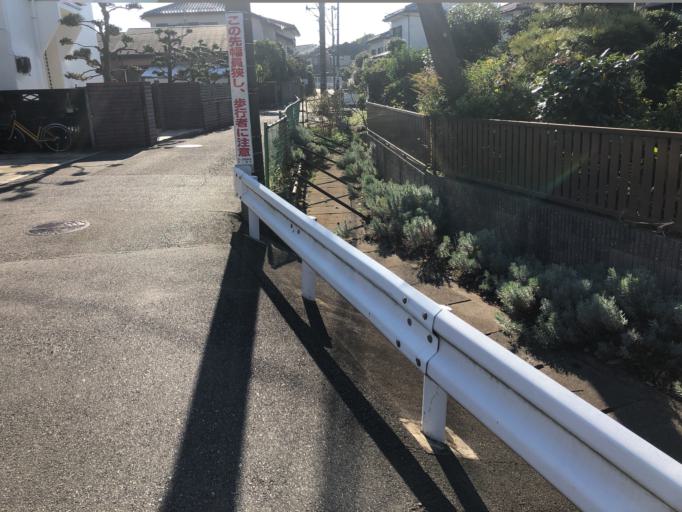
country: JP
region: Kanagawa
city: Chigasaki
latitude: 35.3577
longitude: 139.4048
